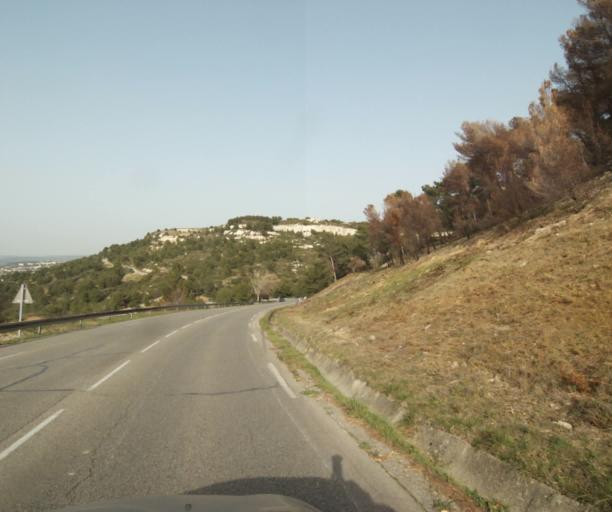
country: FR
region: Provence-Alpes-Cote d'Azur
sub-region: Departement des Bouches-du-Rhone
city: Vitrolles
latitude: 43.4656
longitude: 5.2363
